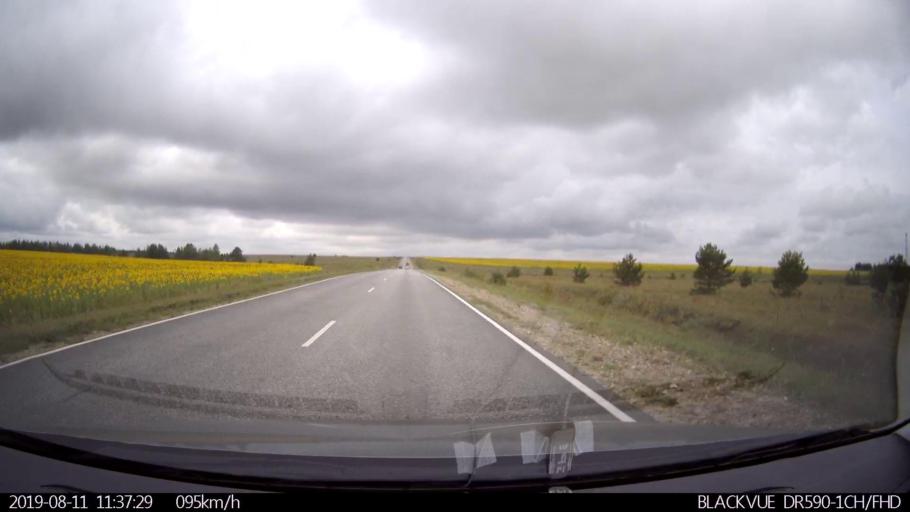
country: RU
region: Ulyanovsk
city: Silikatnyy
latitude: 53.9984
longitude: 48.1959
